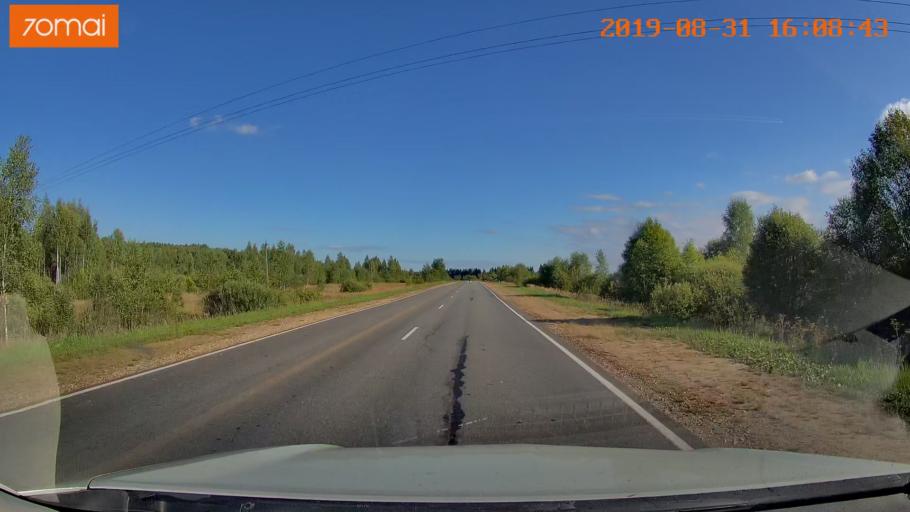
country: RU
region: Kaluga
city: Yukhnov
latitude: 54.5937
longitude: 35.3813
